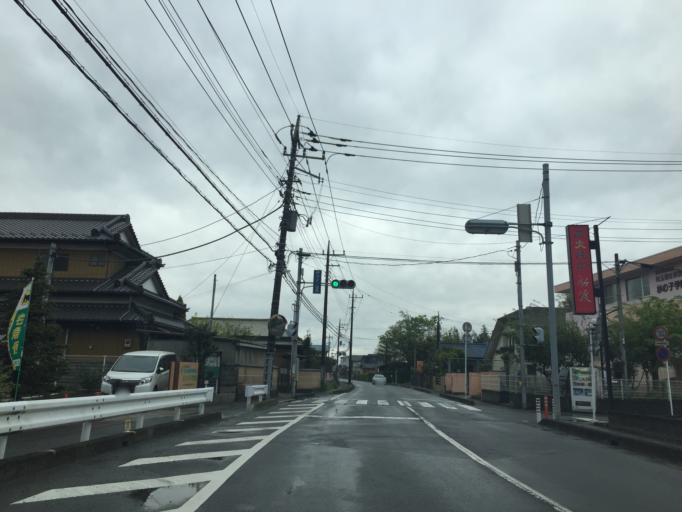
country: JP
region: Saitama
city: Kamifukuoka
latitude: 35.8825
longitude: 139.5605
